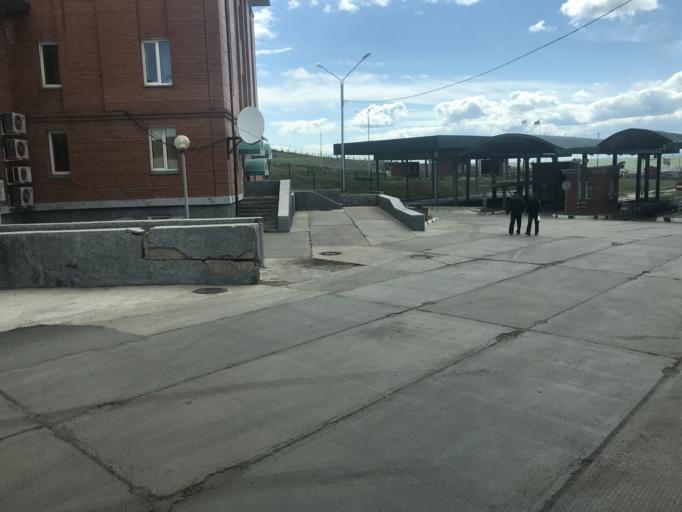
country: MN
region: Selenge
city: Altanbulag
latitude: 50.3257
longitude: 106.4868
